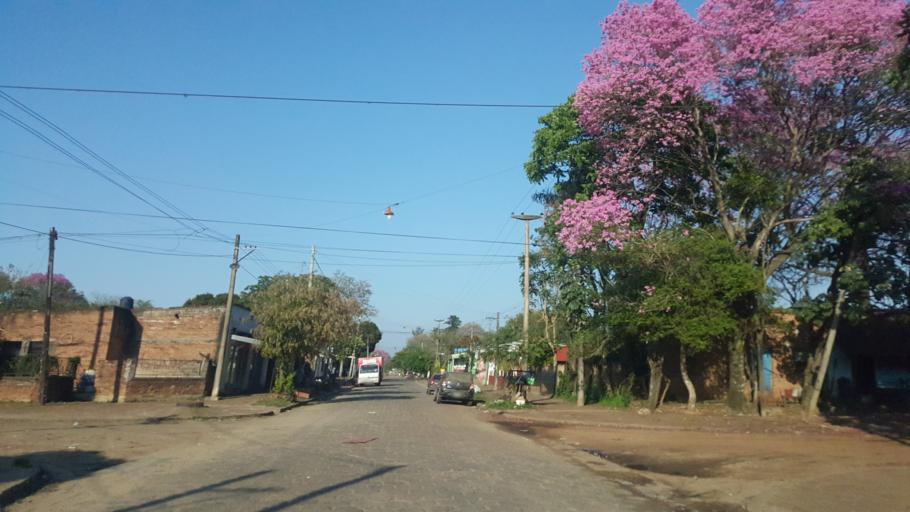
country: AR
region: Corrientes
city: Ituzaingo
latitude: -27.5891
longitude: -56.6923
